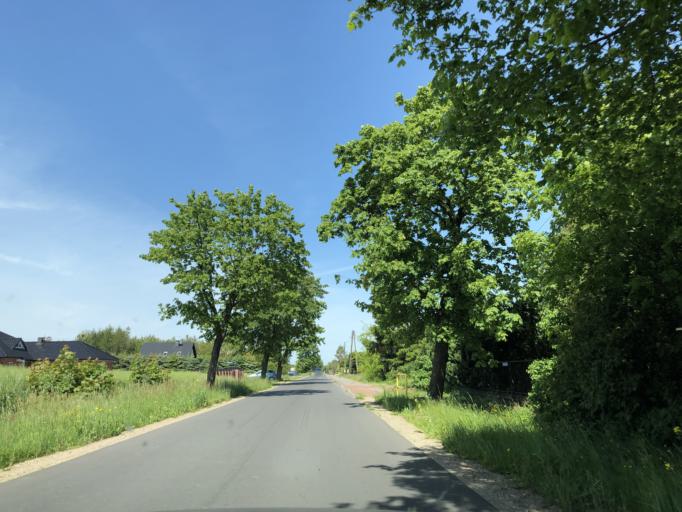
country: PL
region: West Pomeranian Voivodeship
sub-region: Powiat kolobrzeski
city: Dygowo
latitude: 54.1242
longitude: 15.7113
